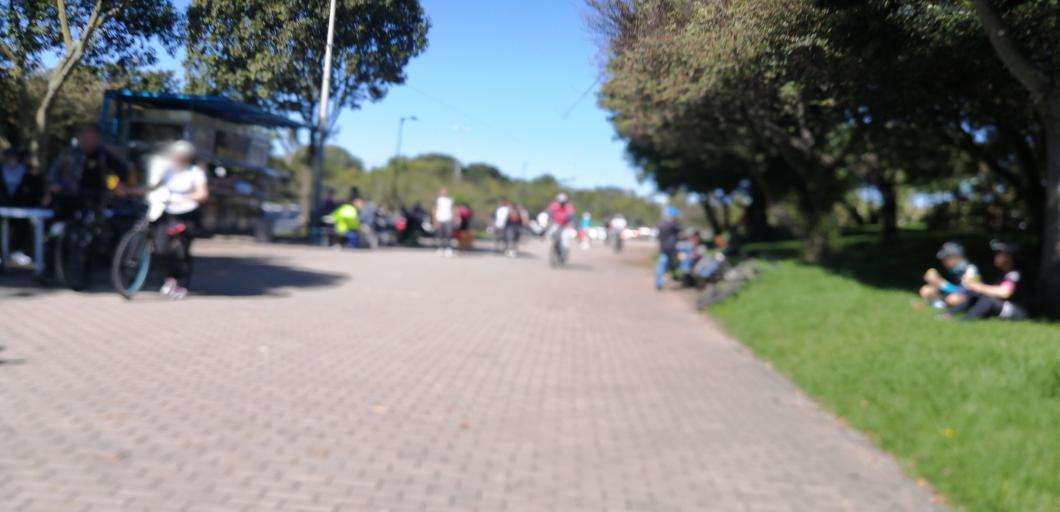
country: CO
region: Bogota D.C.
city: Bogota
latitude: 4.6546
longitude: -74.0919
